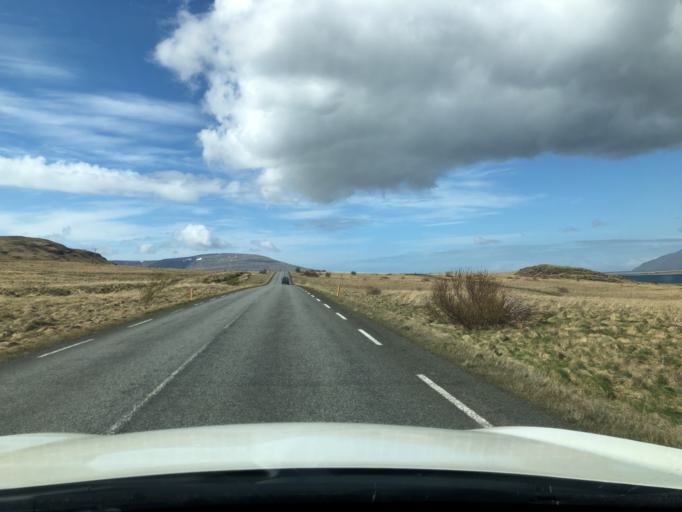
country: IS
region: Capital Region
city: Mosfellsbaer
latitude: 64.3305
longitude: -21.6752
